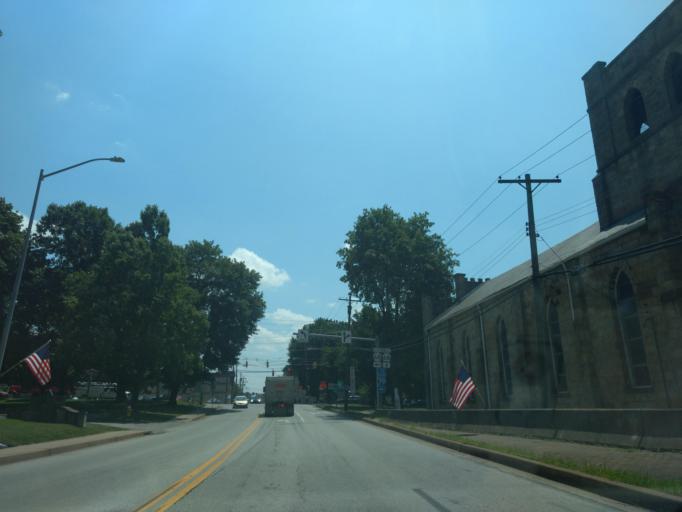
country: US
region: Pennsylvania
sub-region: Butler County
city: Zelienople
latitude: 40.7978
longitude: -80.1375
